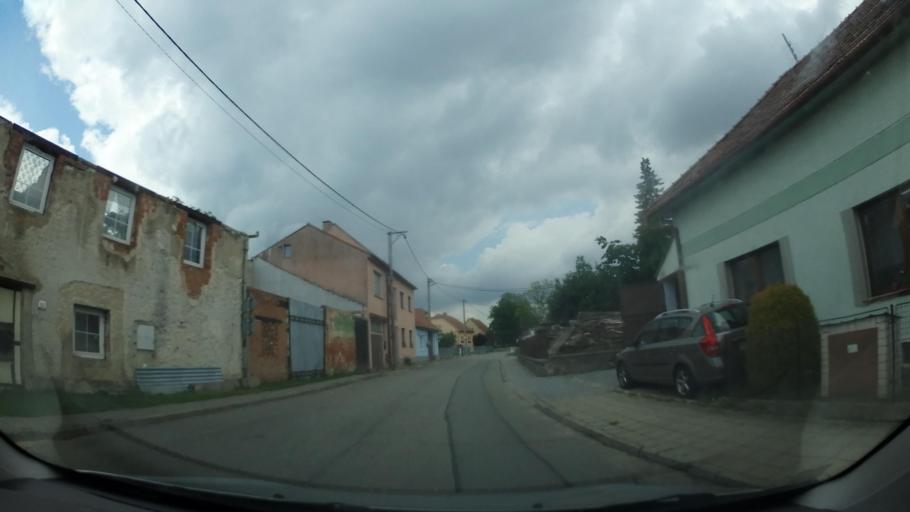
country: CZ
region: South Moravian
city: Boritov
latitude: 49.4524
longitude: 16.6032
